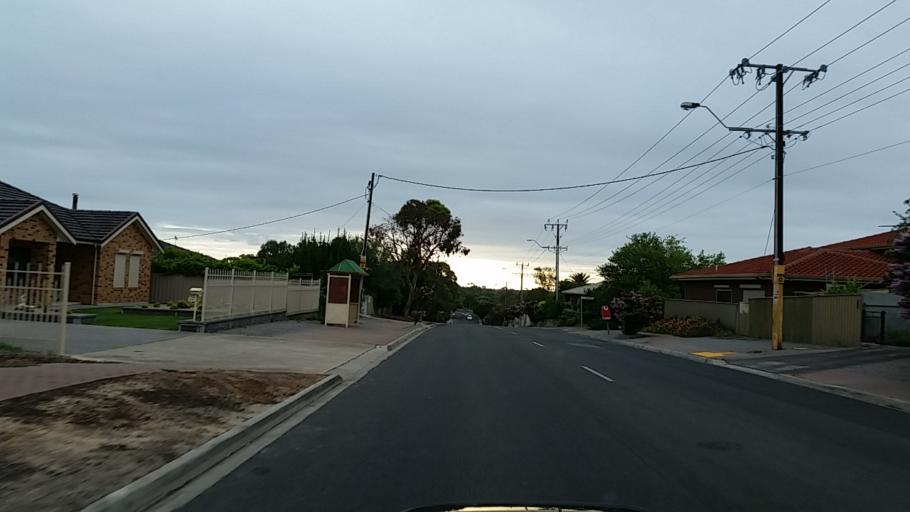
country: AU
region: South Australia
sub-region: Campbelltown
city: Athelstone
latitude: -34.8662
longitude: 138.6974
